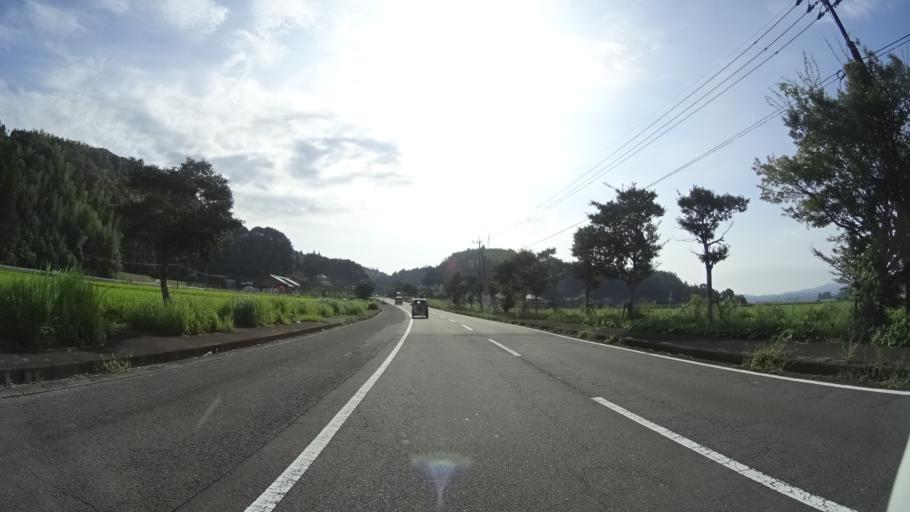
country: JP
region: Kagoshima
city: Okuchi-shinohara
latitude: 32.0185
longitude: 130.6199
